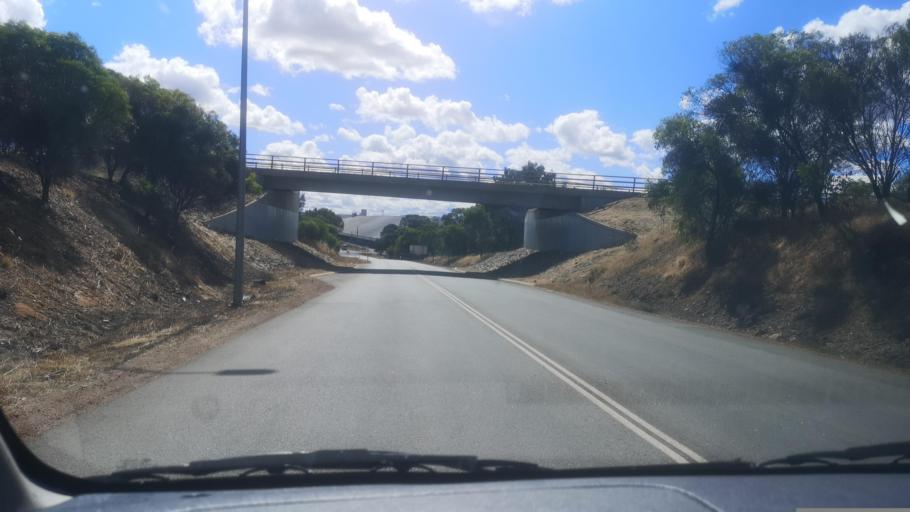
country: AU
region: Western Australia
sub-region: Northam
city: Northam
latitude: -31.6425
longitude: 116.6414
